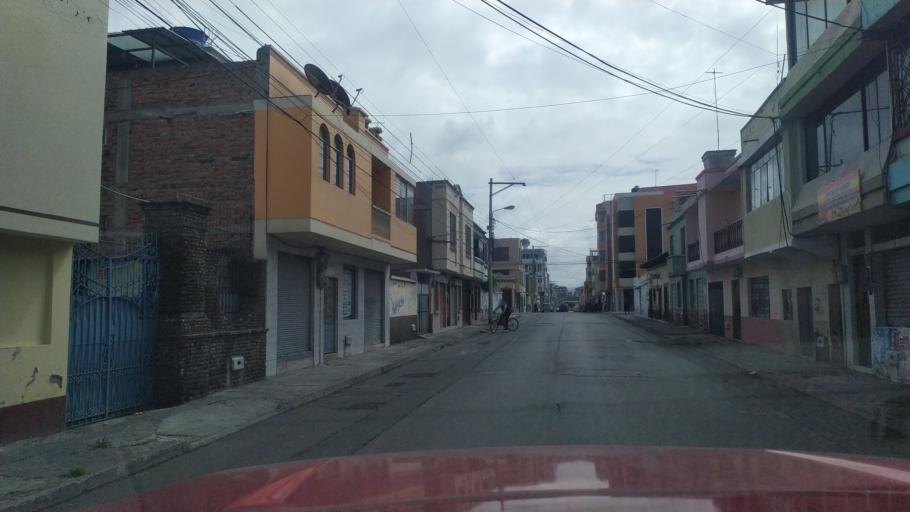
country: EC
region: Chimborazo
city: Riobamba
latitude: -1.6664
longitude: -78.6514
